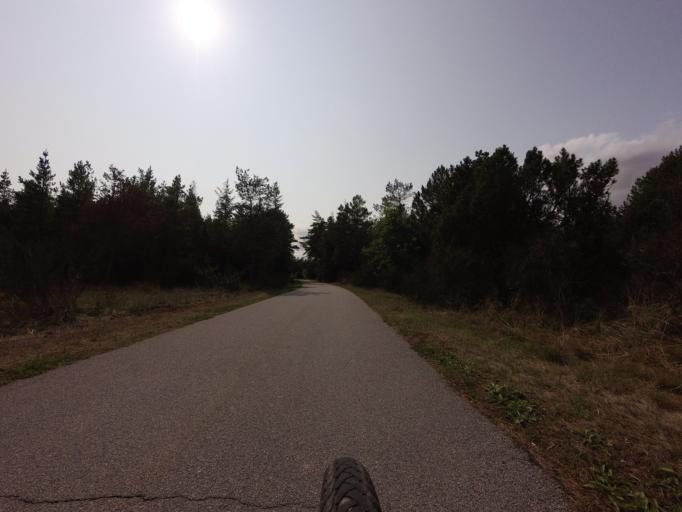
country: DK
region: North Denmark
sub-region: Frederikshavn Kommune
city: Strandby
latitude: 57.6426
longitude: 10.4369
